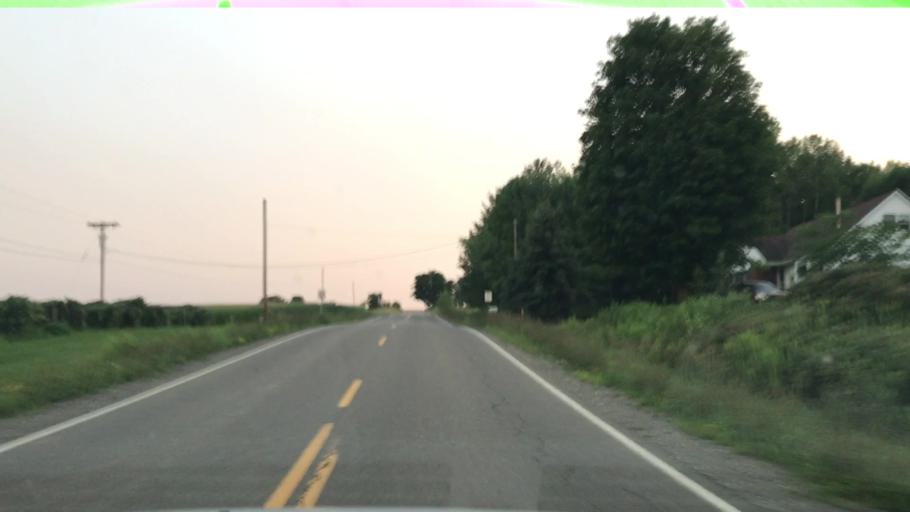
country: US
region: New York
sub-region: Steuben County
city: Sylvan Beach
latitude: 42.5194
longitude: -77.1711
